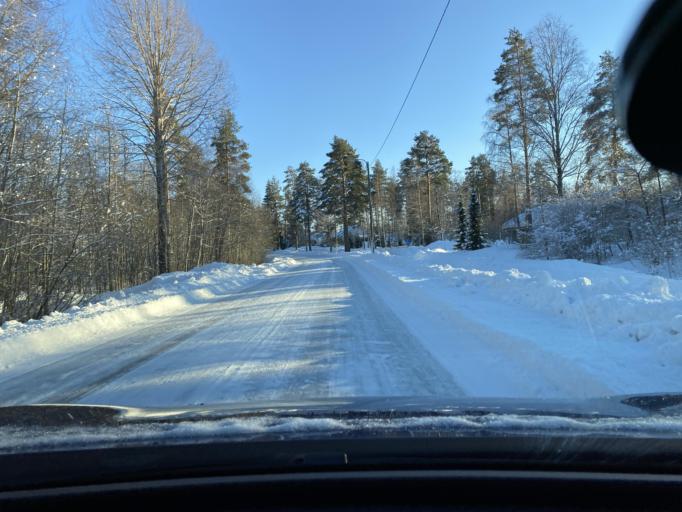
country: FI
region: Southern Savonia
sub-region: Mikkeli
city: Kangasniemi
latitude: 62.0024
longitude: 26.6245
